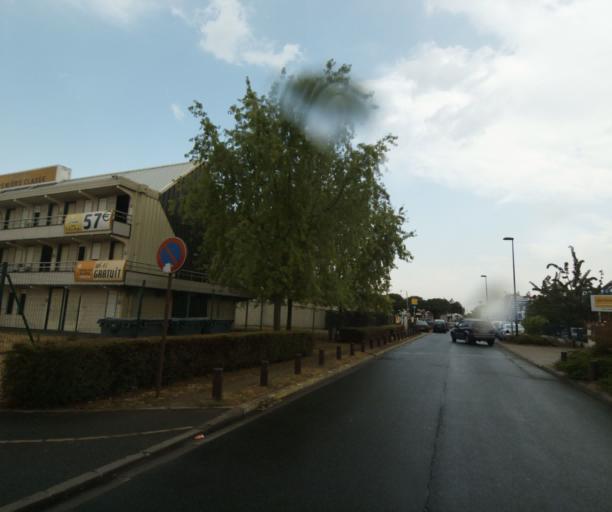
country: FR
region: Ile-de-France
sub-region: Departement des Yvelines
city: Conflans-Sainte-Honorine
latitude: 49.0098
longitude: 2.0855
